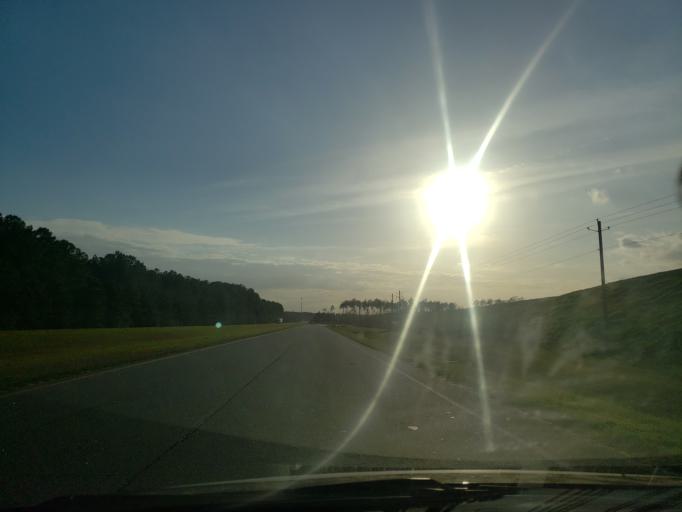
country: US
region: Georgia
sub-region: Chatham County
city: Bloomingdale
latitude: 32.1585
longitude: -81.2716
